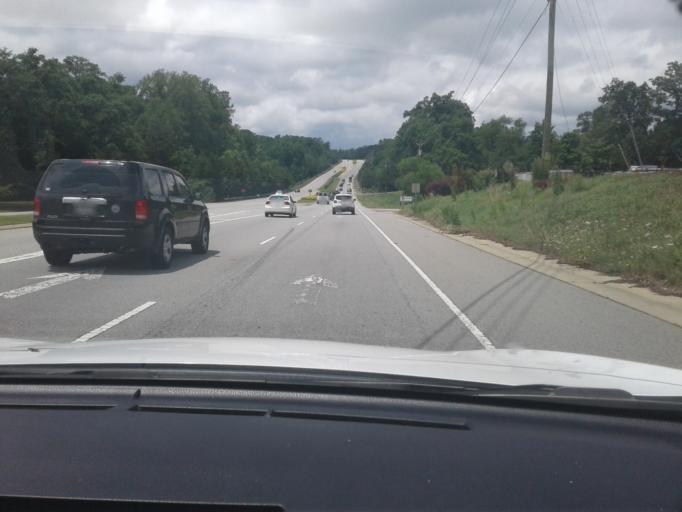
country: US
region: North Carolina
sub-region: Wake County
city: Fuquay-Varina
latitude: 35.6185
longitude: -78.8151
